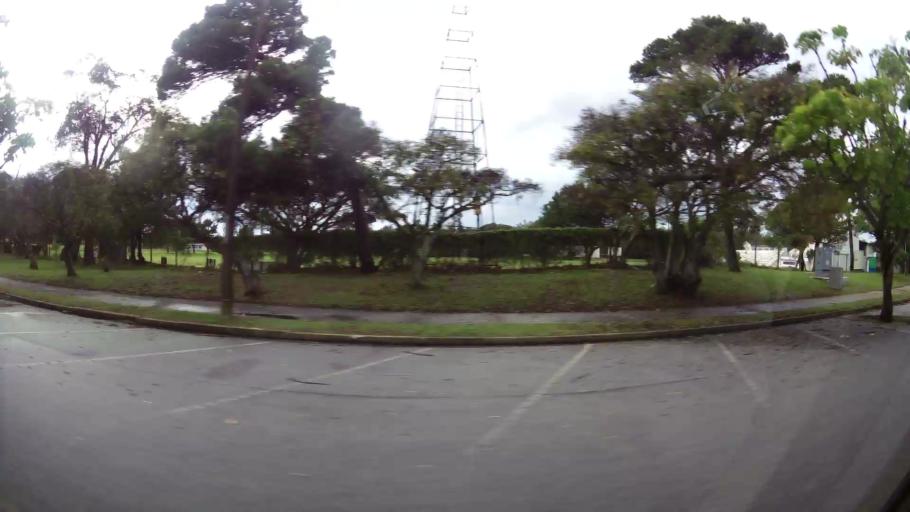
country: ZA
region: Eastern Cape
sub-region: Nelson Mandela Bay Metropolitan Municipality
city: Port Elizabeth
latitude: -33.9652
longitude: 25.6034
